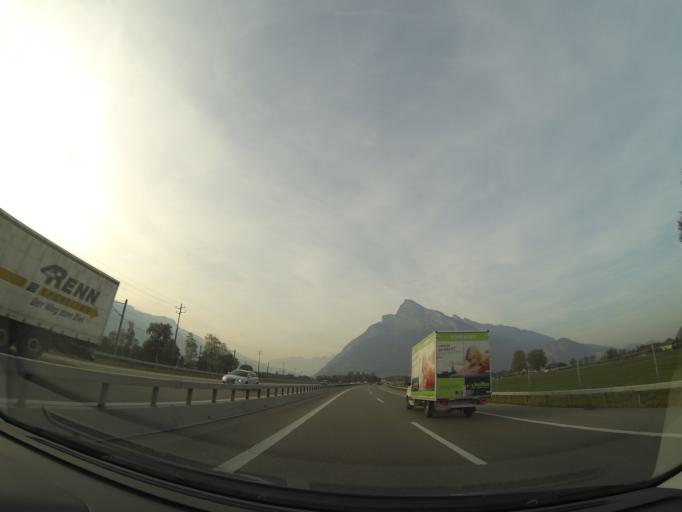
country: CH
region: Saint Gallen
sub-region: Wahlkreis Sarganserland
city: Sargans
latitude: 47.0313
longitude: 9.4694
